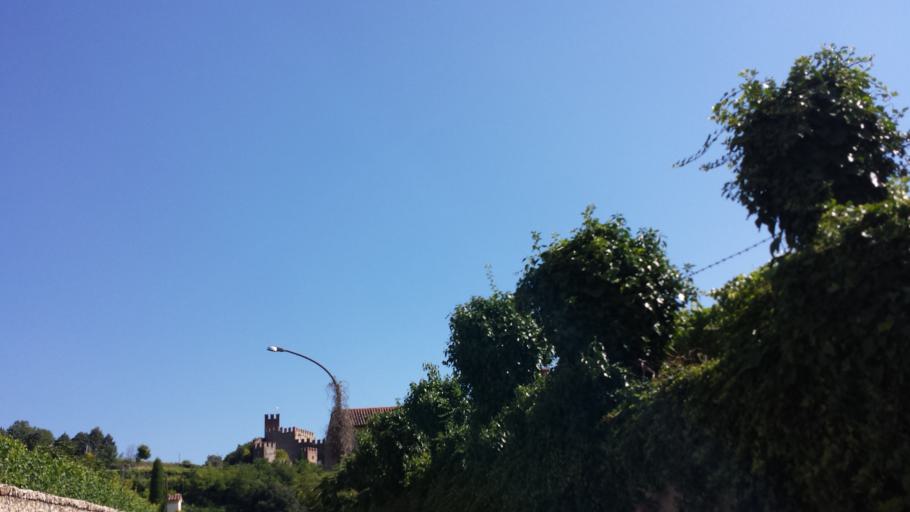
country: IT
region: Veneto
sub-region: Provincia di Verona
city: Soave
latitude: 45.4270
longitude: 11.2492
